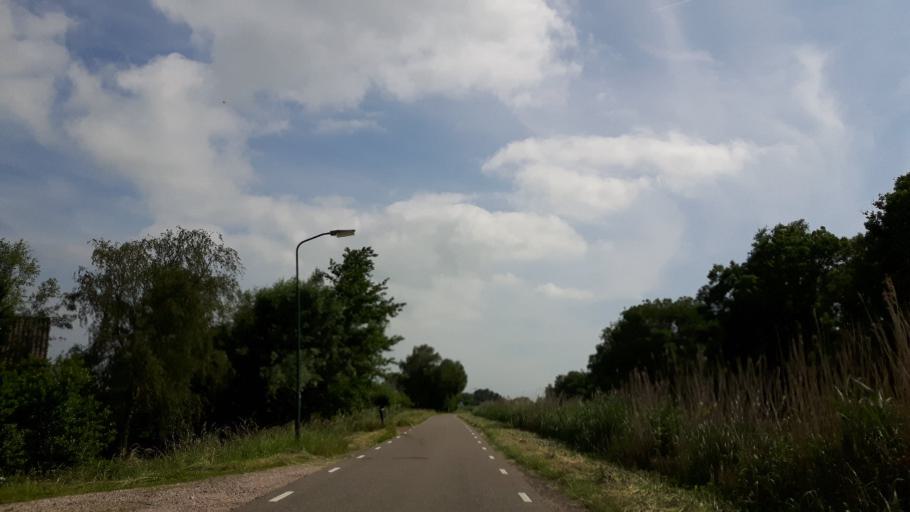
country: NL
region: Utrecht
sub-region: Gemeente De Ronde Venen
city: Mijdrecht
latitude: 52.1689
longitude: 4.8686
